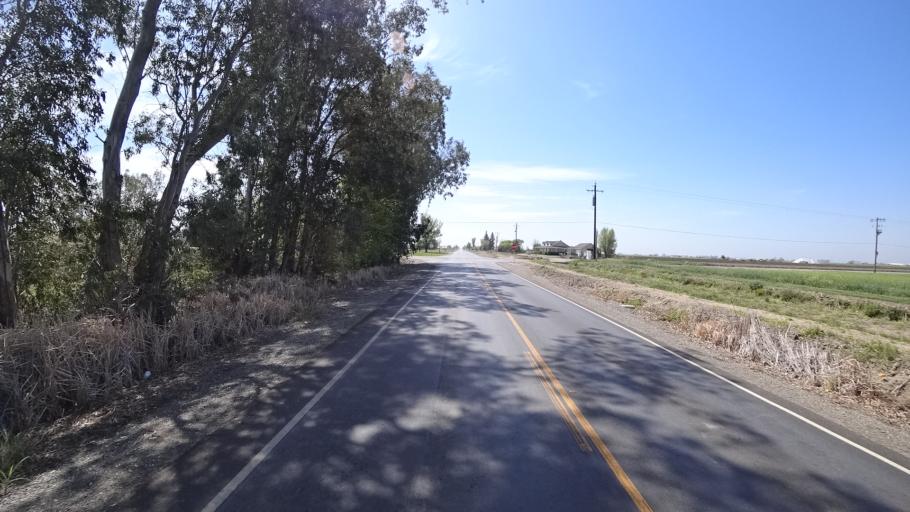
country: US
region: California
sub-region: Glenn County
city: Willows
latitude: 39.5833
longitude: -122.0652
